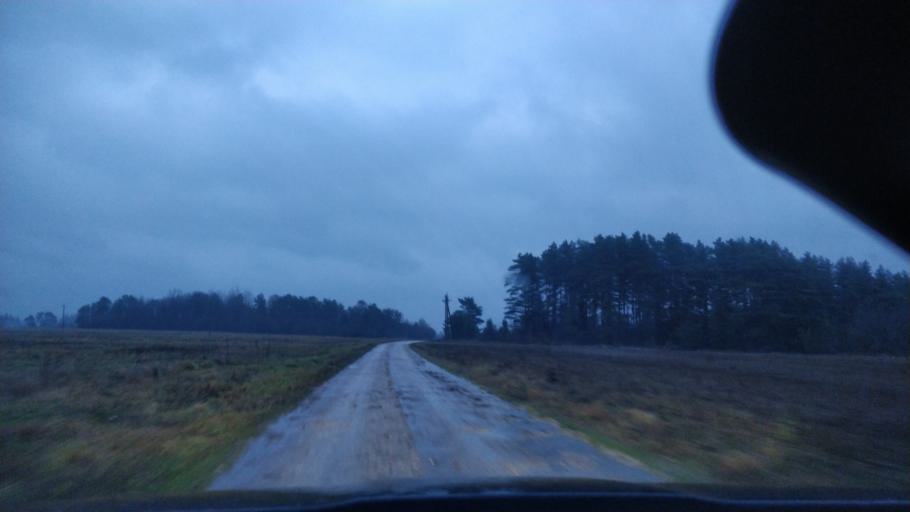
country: EE
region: Laeaene
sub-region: Lihula vald
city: Lihula
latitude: 58.8513
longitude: 23.9923
